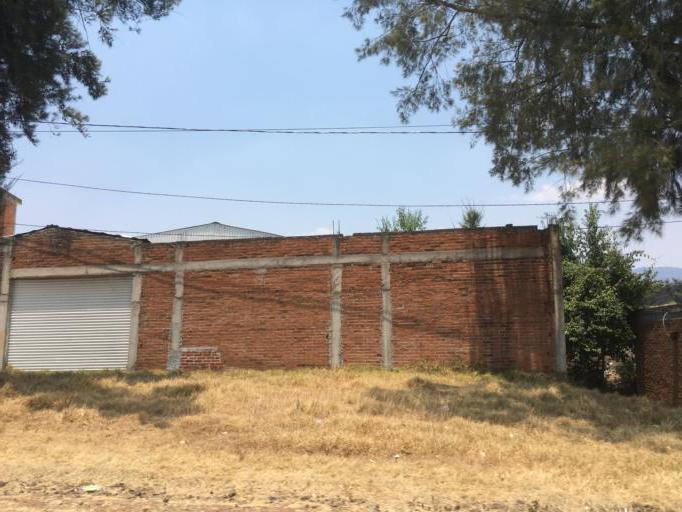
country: MX
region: Michoacan
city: Quiroga
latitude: 19.6471
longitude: -101.4919
